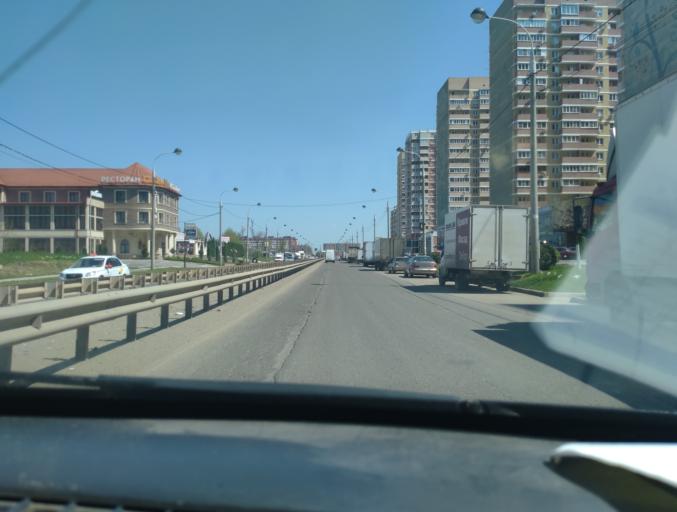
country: RU
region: Krasnodarskiy
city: Krasnodar
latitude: 45.0944
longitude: 39.0071
